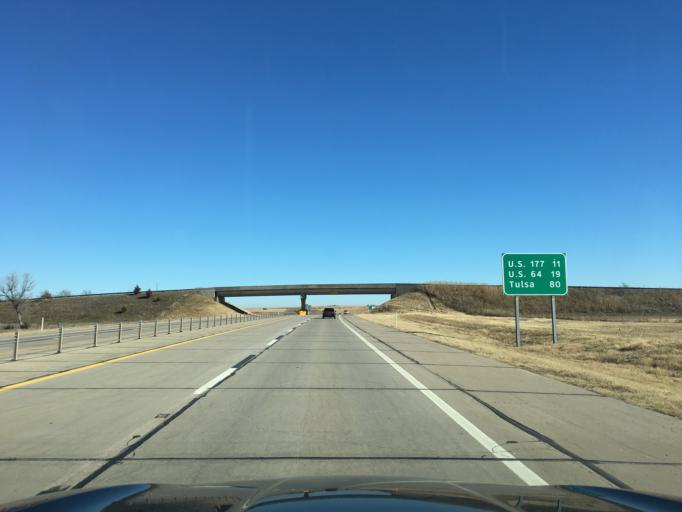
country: US
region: Oklahoma
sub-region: Noble County
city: Perry
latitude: 36.4012
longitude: -97.2668
